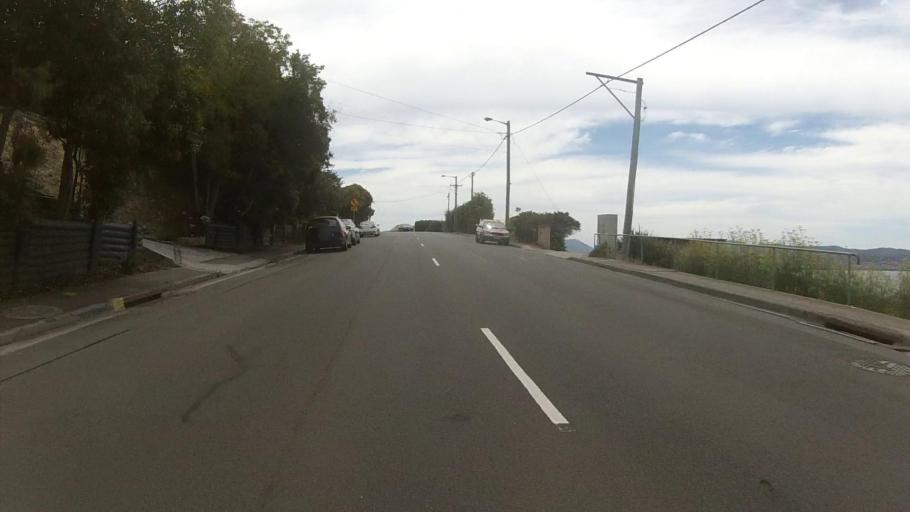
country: AU
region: Tasmania
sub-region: Kingborough
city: Taroona
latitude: -42.9168
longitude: 147.3454
